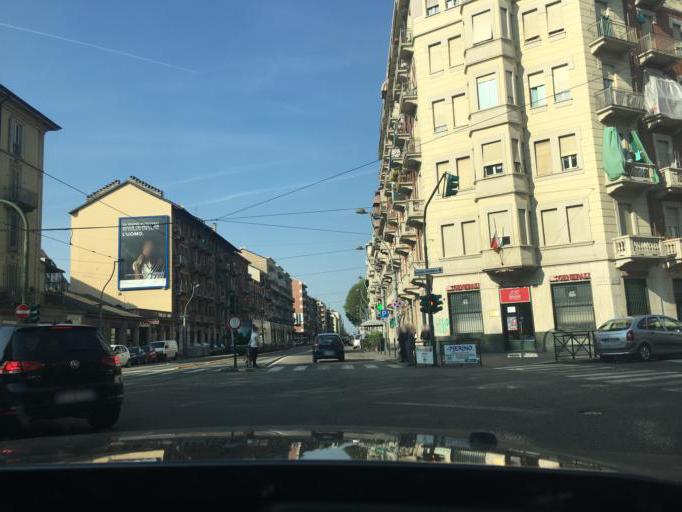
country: IT
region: Piedmont
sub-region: Provincia di Torino
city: Turin
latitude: 45.0925
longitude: 7.6940
